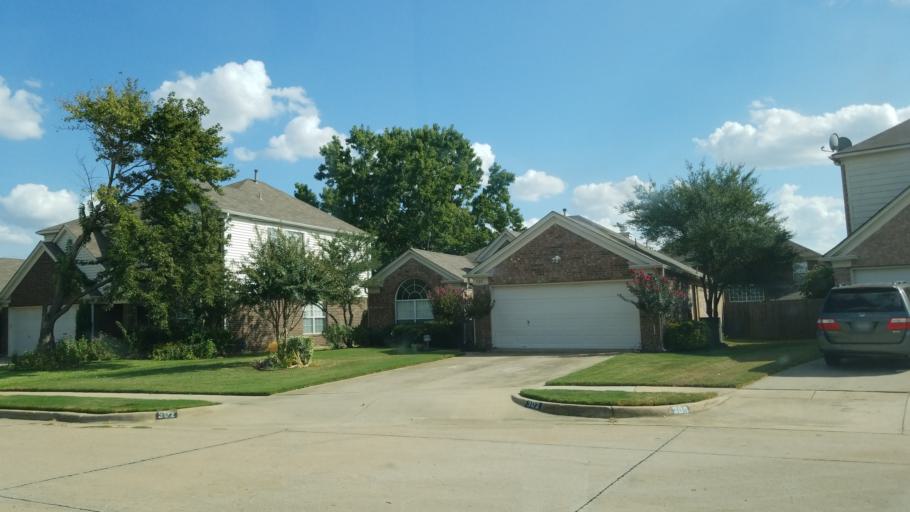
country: US
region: Texas
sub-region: Tarrant County
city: Euless
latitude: 32.8504
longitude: -97.0783
